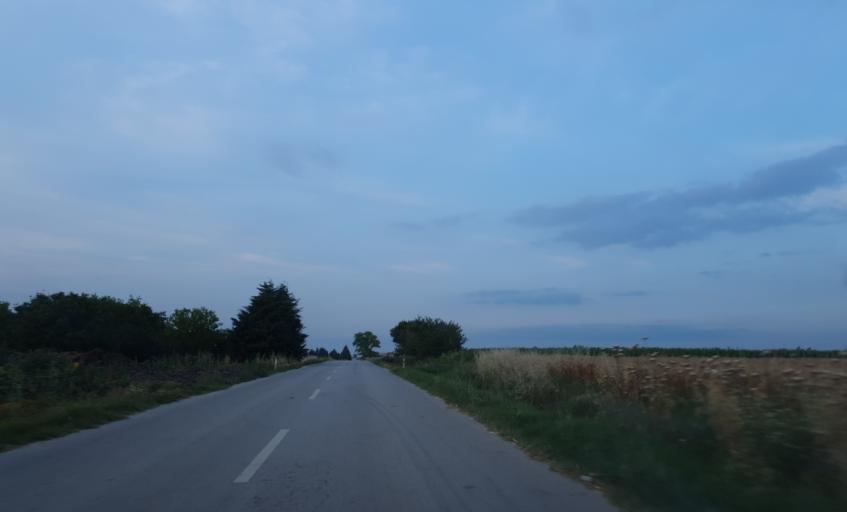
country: TR
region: Tekirdag
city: Beyazkoy
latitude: 41.3904
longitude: 27.6263
